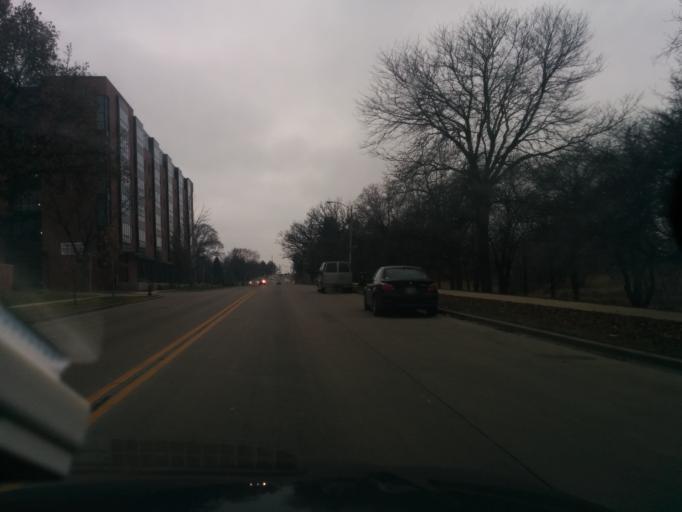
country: US
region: Wisconsin
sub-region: Milwaukee County
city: Wauwatosa
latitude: 43.0385
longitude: -88.0228
